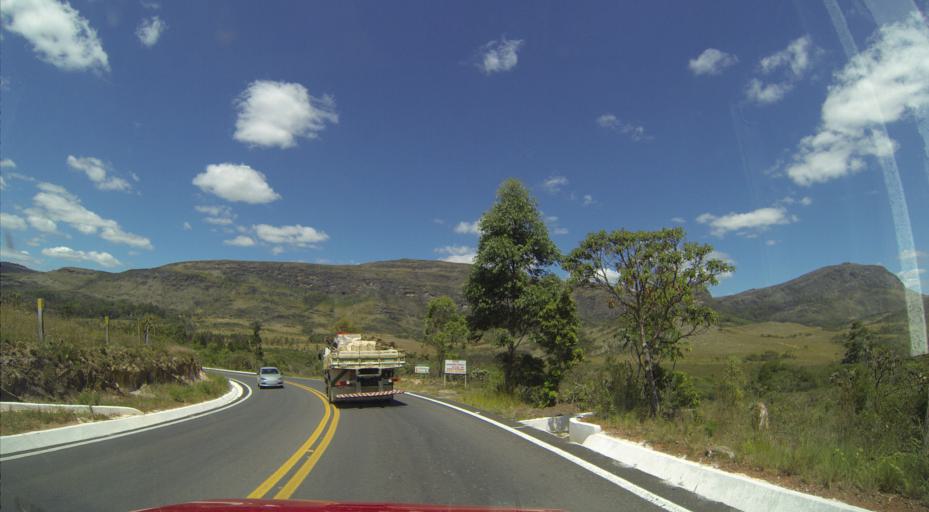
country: BR
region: Minas Gerais
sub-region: Conceicao Do Mato Dentro
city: Conceicao do Mato Dentro
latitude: -19.2889
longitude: -43.5552
